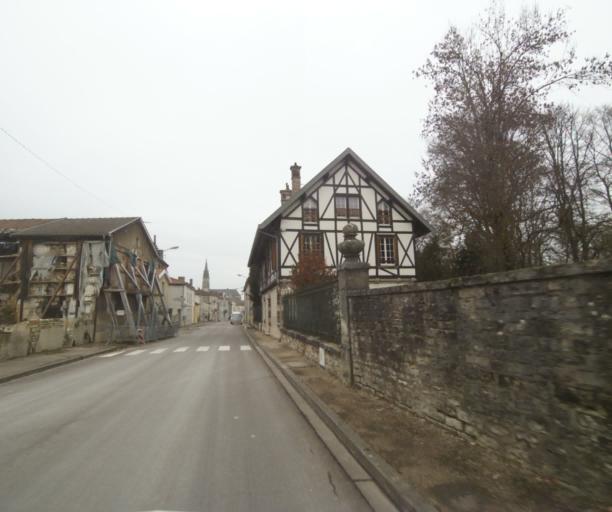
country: FR
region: Champagne-Ardenne
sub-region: Departement de la Haute-Marne
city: Bienville
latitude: 48.5825
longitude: 5.0391
